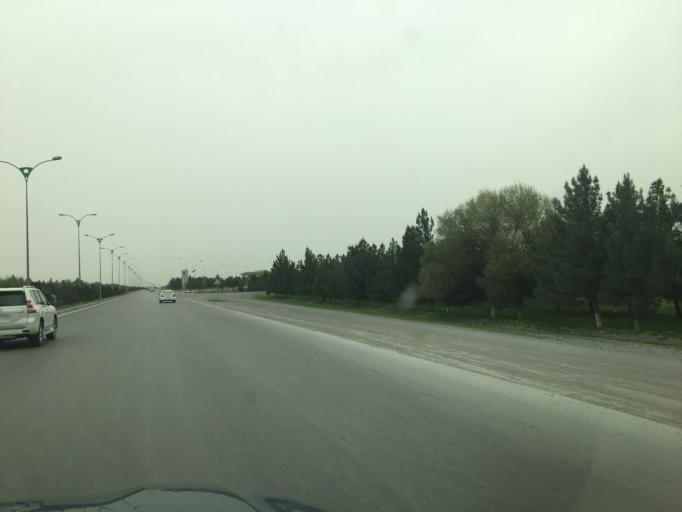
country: TM
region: Ahal
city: Abadan
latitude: 38.1462
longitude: 57.9897
